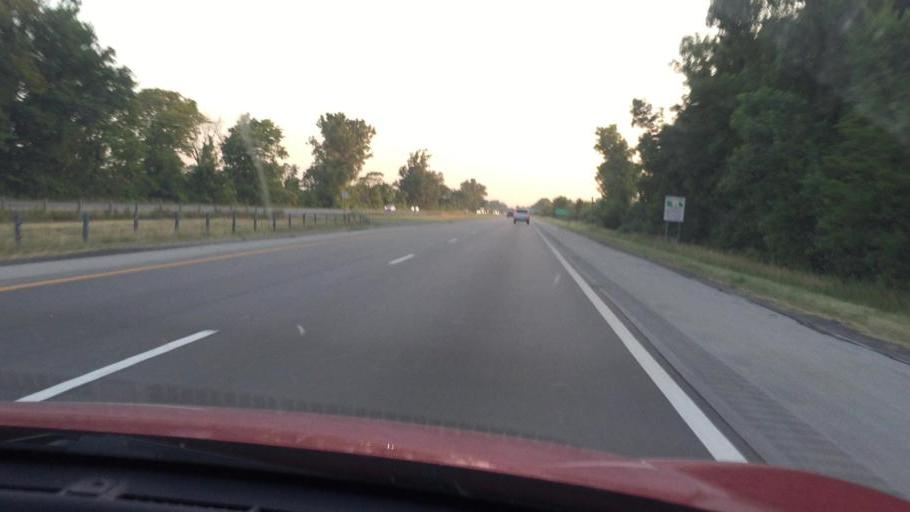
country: US
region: Michigan
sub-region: Washtenaw County
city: Milan
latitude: 42.0544
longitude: -83.6699
